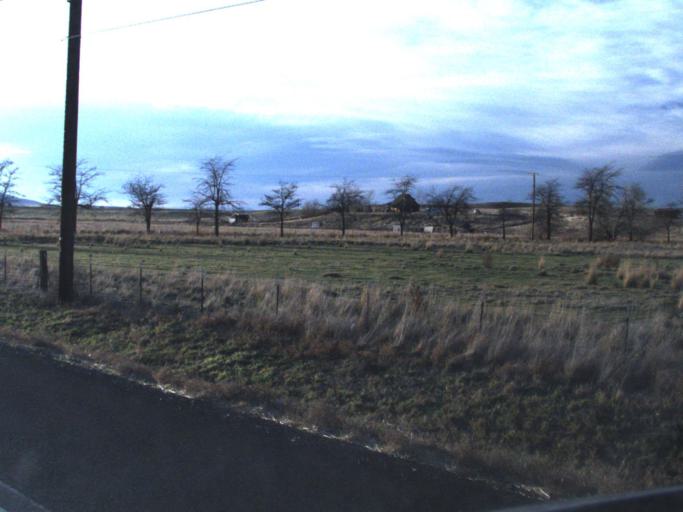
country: US
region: Washington
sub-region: Walla Walla County
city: Garrett
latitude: 46.0490
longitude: -118.6309
